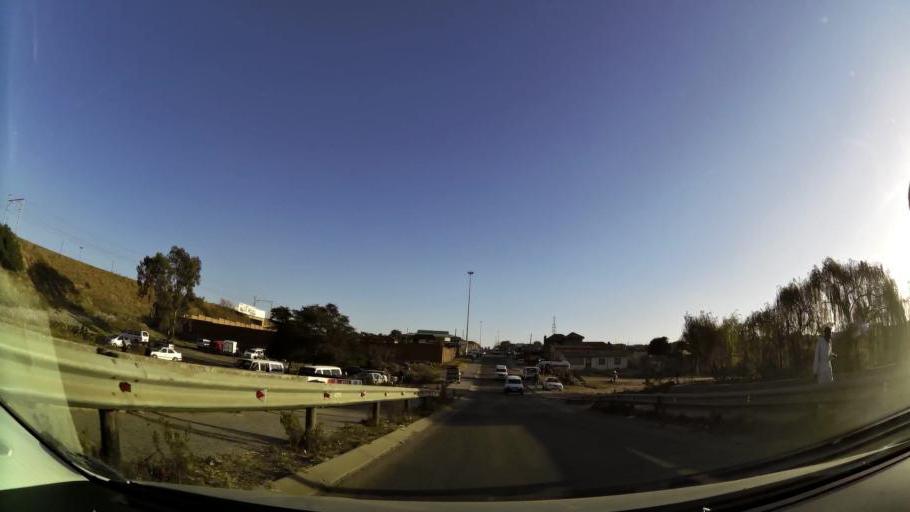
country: ZA
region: Gauteng
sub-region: Ekurhuleni Metropolitan Municipality
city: Tembisa
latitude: -26.0223
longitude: 28.2042
